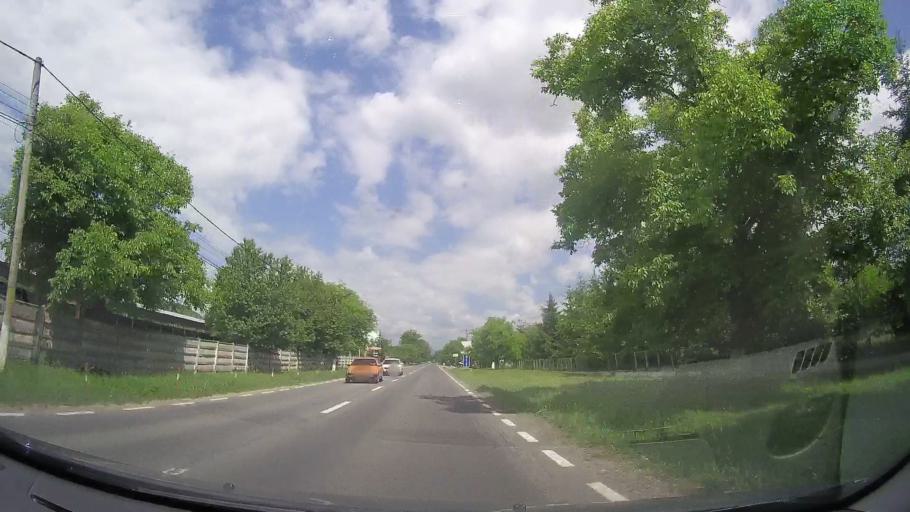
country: RO
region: Prahova
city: Drajna de Jos
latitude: 45.2127
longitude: 26.0386
